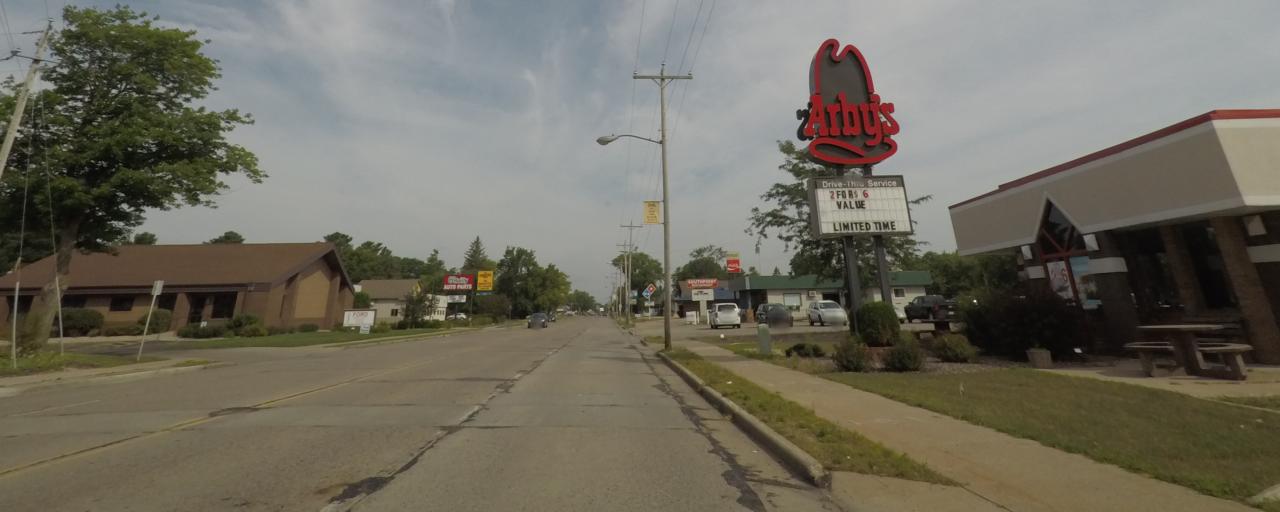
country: US
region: Wisconsin
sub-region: Portage County
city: Whiting
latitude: 44.5054
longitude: -89.5673
